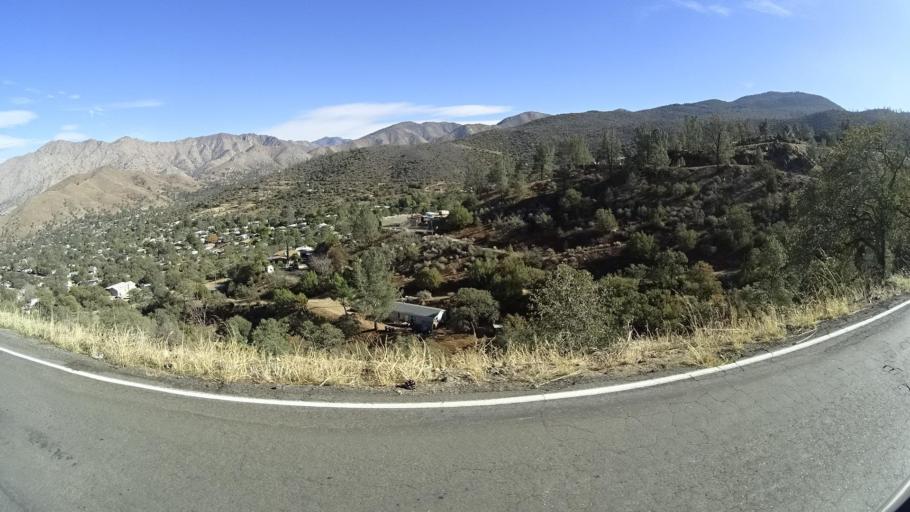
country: US
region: California
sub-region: Kern County
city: Bodfish
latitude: 35.5837
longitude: -118.5020
